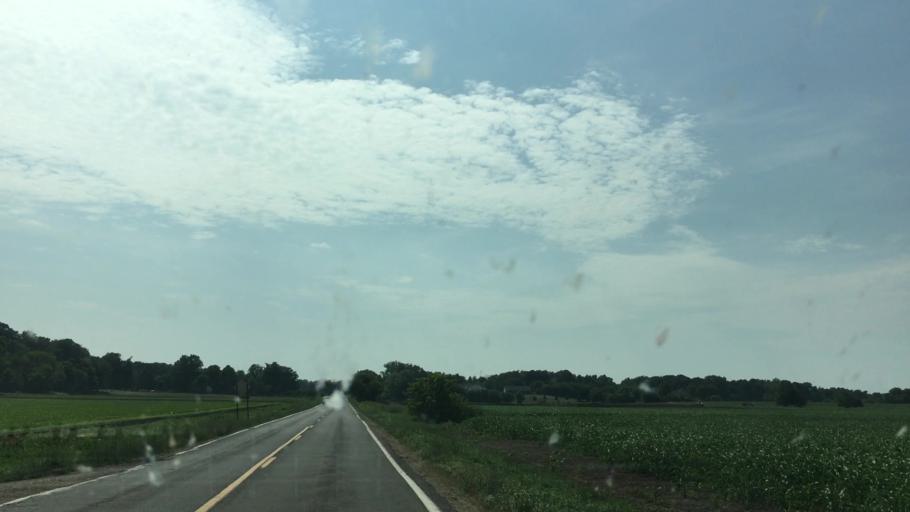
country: US
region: Michigan
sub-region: Kent County
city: Byron Center
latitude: 42.7829
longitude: -85.7639
